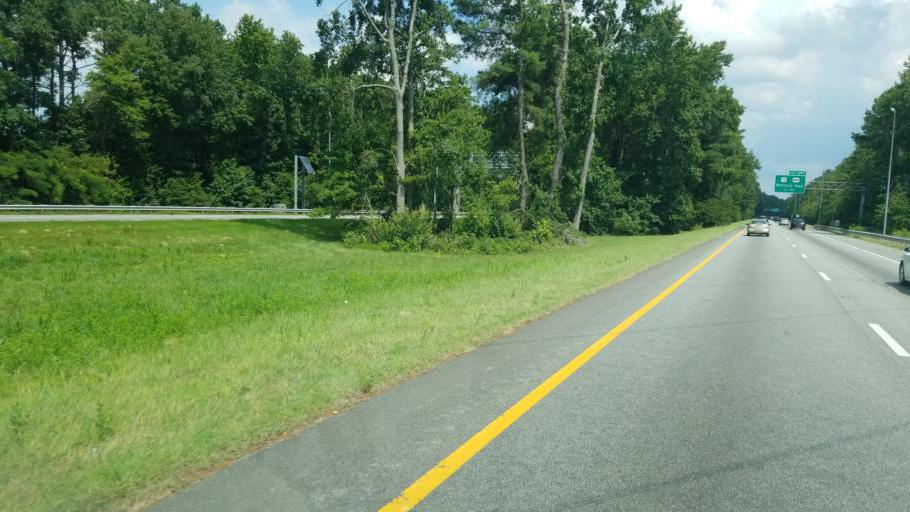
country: US
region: Virginia
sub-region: City of Portsmouth
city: Portsmouth Heights
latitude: 36.7771
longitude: -76.3795
